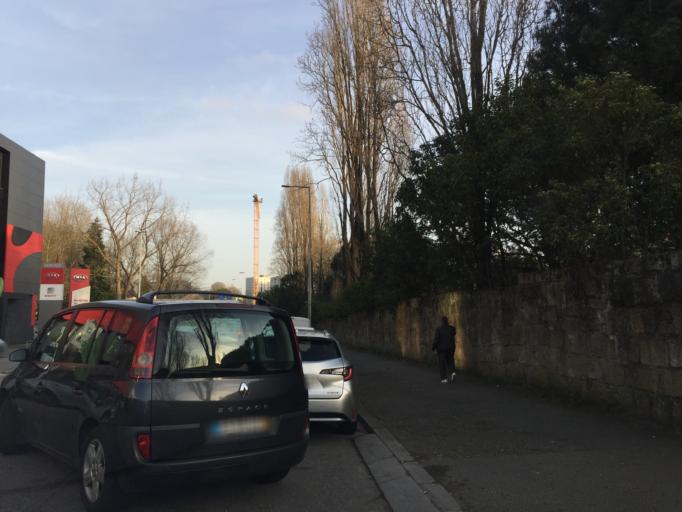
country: PT
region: Porto
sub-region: Matosinhos
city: Senhora da Hora
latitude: 41.1696
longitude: -8.6467
